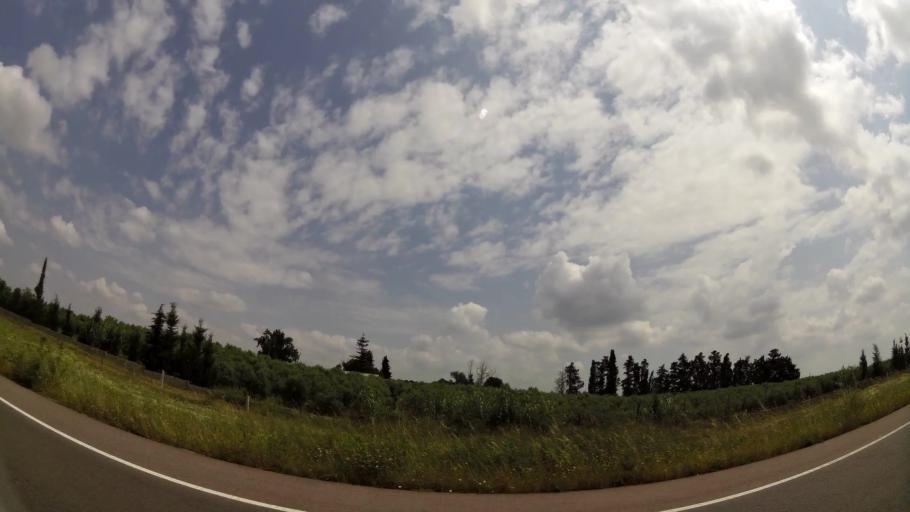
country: MA
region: Rabat-Sale-Zemmour-Zaer
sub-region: Khemisset
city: Tiflet
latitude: 33.9847
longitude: -6.5323
